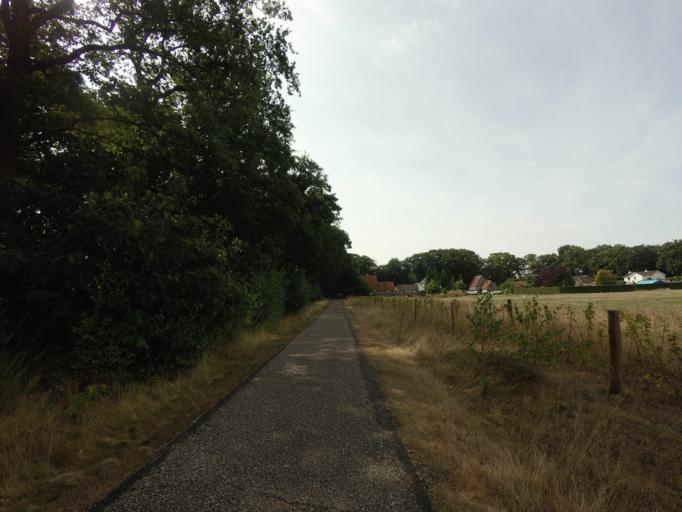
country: NL
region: North Brabant
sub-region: Gemeente Sint Anthonis
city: Sint Anthonis
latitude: 51.5550
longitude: 5.8109
